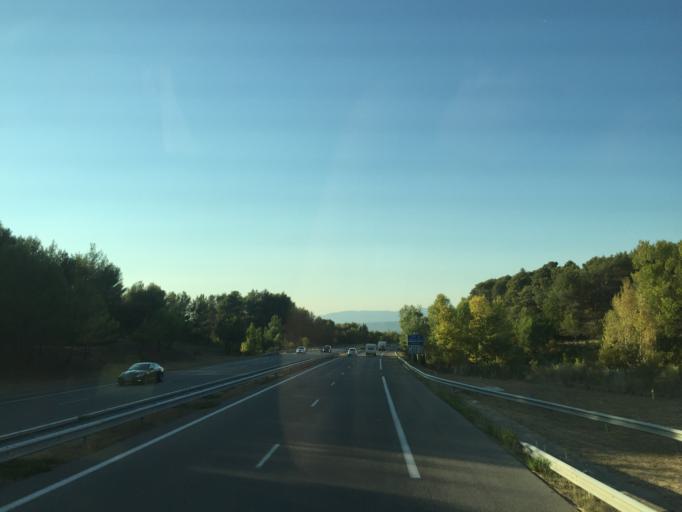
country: FR
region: Provence-Alpes-Cote d'Azur
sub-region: Departement des Bouches-du-Rhone
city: Venelles
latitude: 43.6207
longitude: 5.4937
